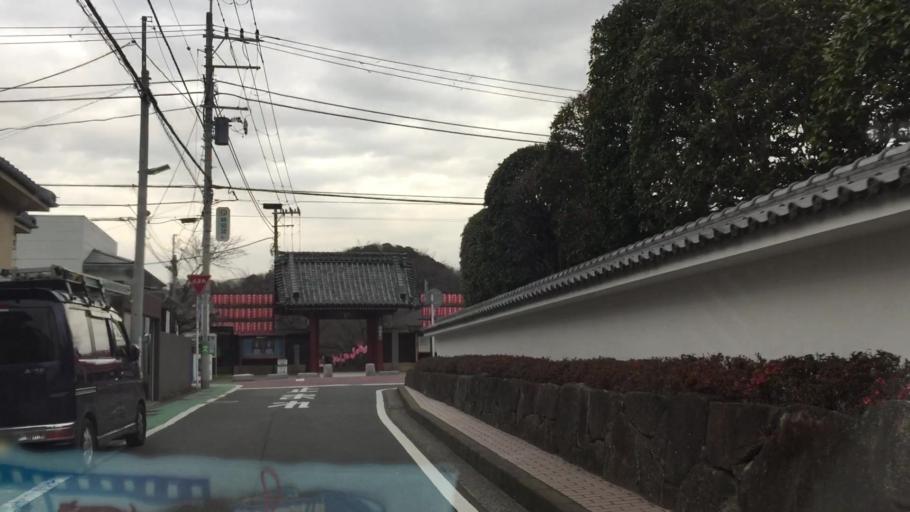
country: JP
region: Kanagawa
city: Yokosuka
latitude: 35.3415
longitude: 139.6294
